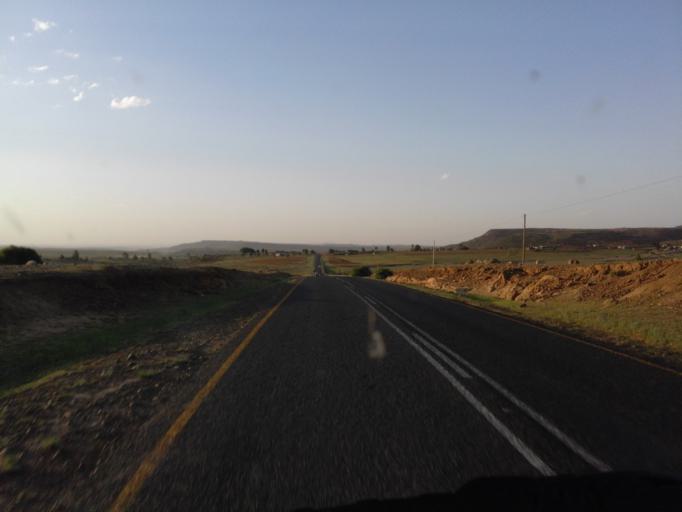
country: LS
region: Mafeteng
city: Mafeteng
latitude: -29.8902
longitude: 27.2532
